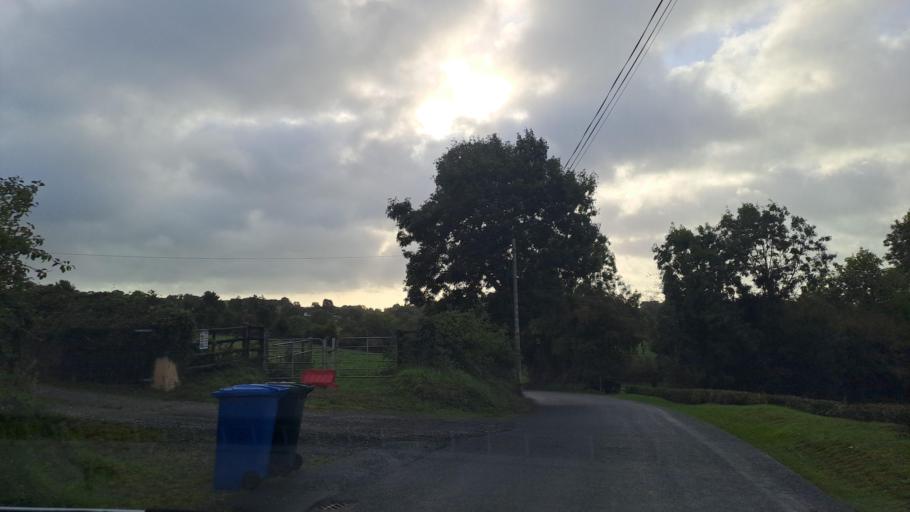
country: IE
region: Ulster
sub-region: An Cabhan
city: Kingscourt
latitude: 53.9546
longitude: -6.7877
